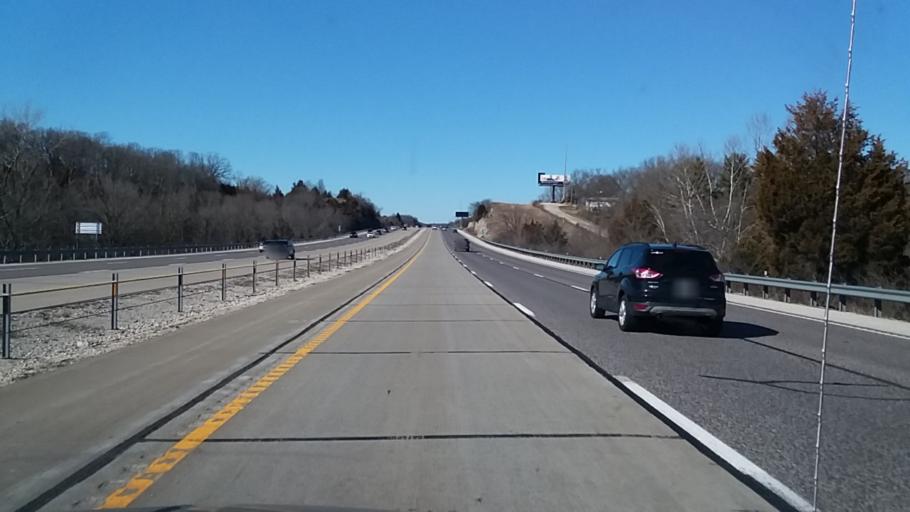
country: US
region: Missouri
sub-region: Jefferson County
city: Barnhart
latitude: 38.3158
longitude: -90.4017
